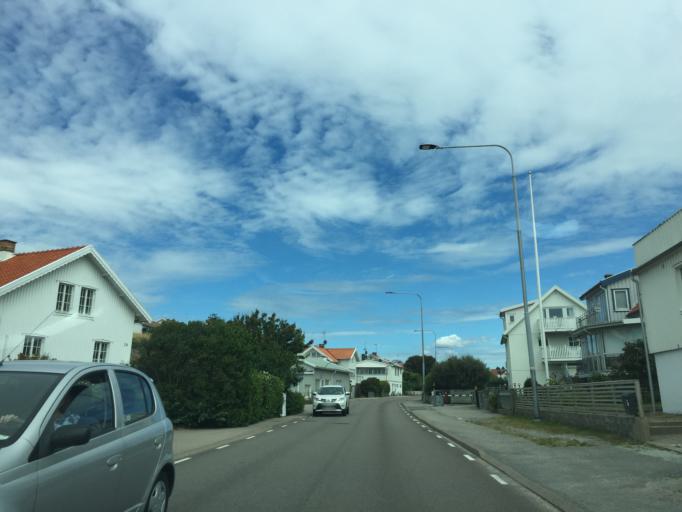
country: SE
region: Vaestra Goetaland
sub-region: Tjorns Kommun
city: Skaerhamn
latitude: 57.9942
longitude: 11.5514
